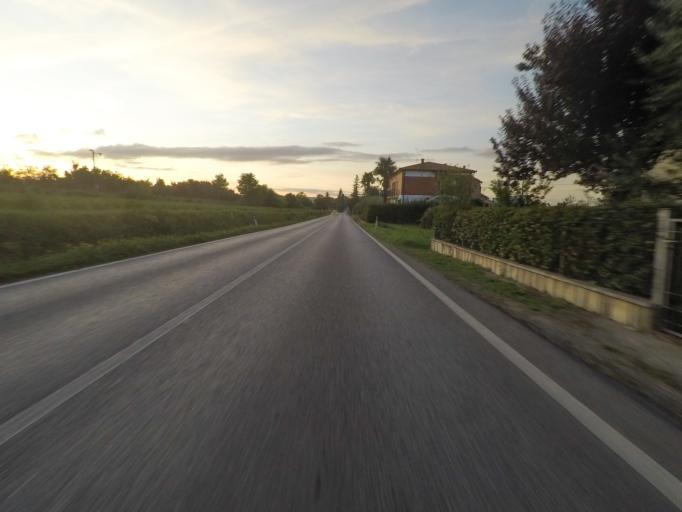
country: IT
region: Tuscany
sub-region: Provincia di Siena
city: Torrita di Siena
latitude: 43.1844
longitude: 11.7678
